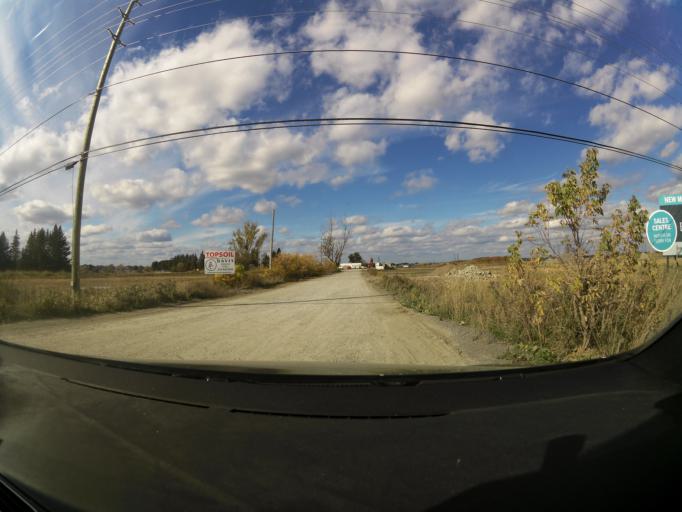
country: CA
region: Ontario
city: Bells Corners
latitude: 45.2683
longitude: -75.8786
